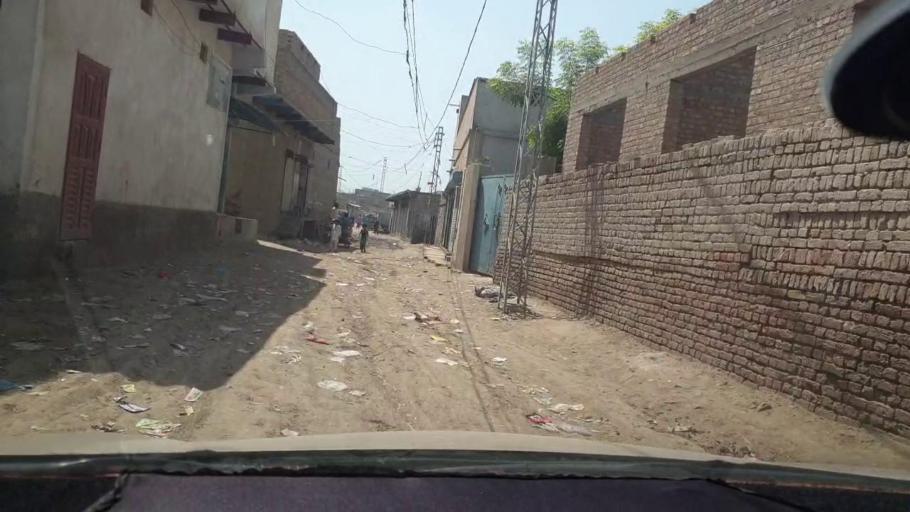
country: PK
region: Sindh
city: Kambar
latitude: 27.6164
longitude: 68.0055
